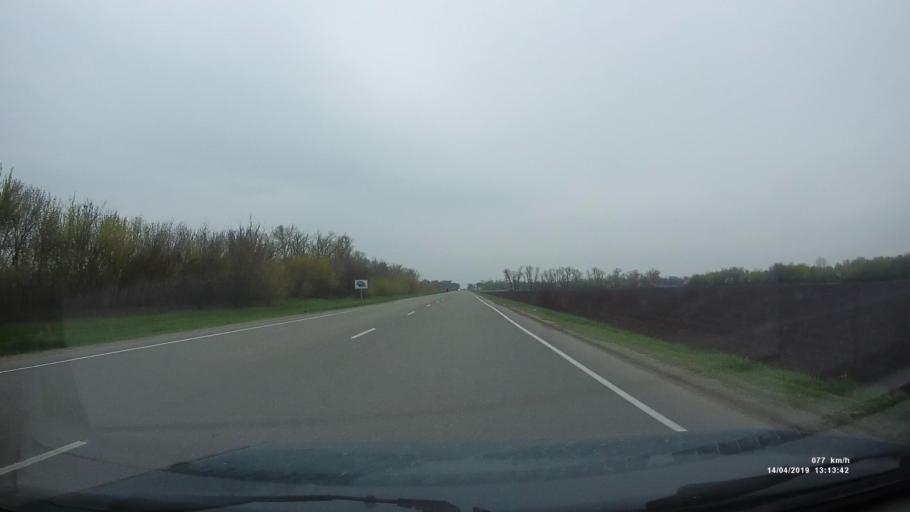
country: RU
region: Rostov
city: Kuleshovka
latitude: 47.0953
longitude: 39.6199
